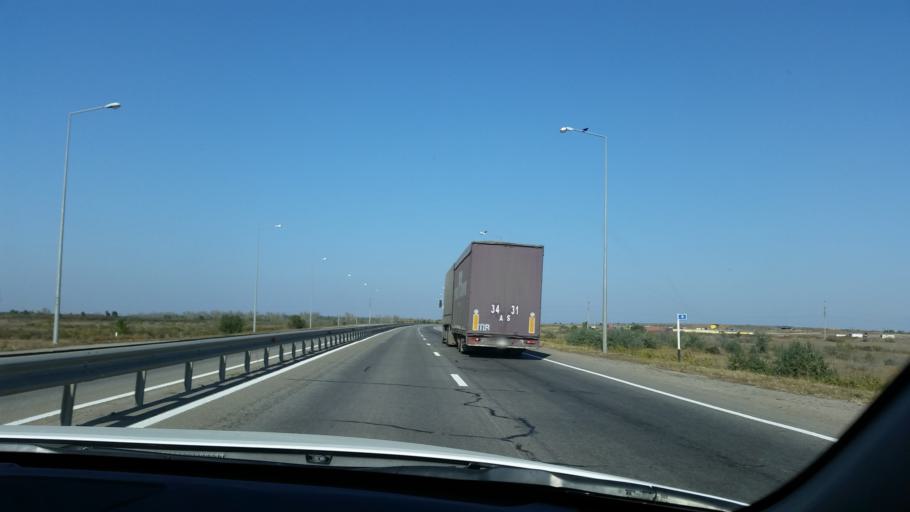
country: KZ
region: Astana Qalasy
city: Astana
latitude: 51.2435
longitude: 71.3355
